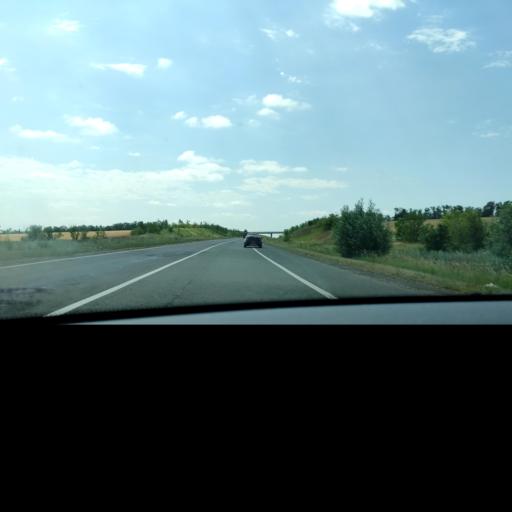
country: RU
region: Samara
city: Petra-Dubrava
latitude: 53.3036
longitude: 50.4141
